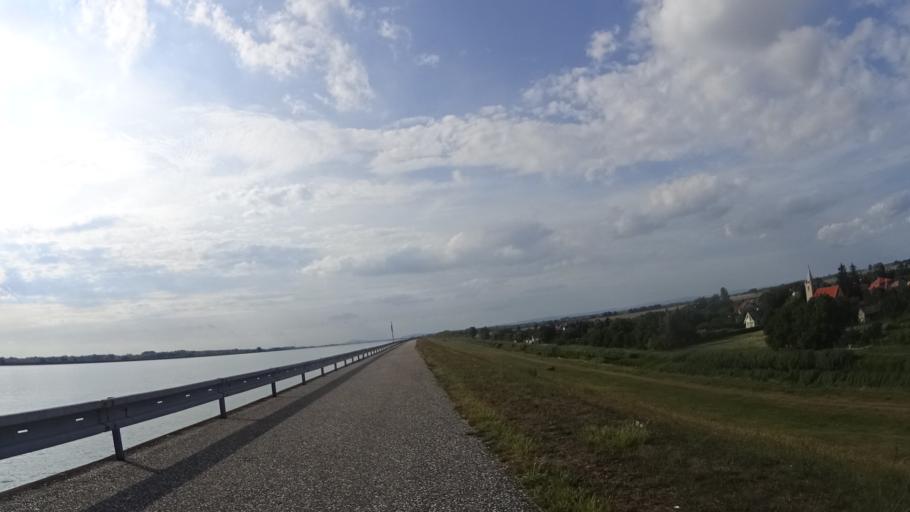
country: HU
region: Gyor-Moson-Sopron
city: Halaszi
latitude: 47.9487
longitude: 17.4413
